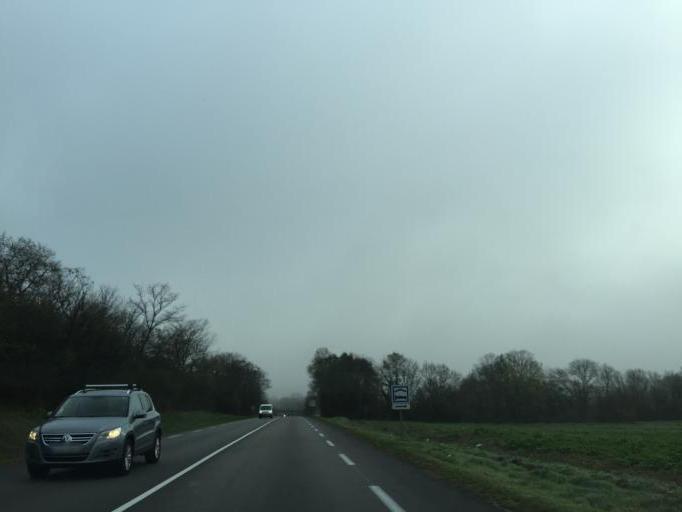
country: FR
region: Rhone-Alpes
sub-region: Departement de l'Ain
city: Saint-Jean-de-Niost
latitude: 45.8568
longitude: 5.2169
